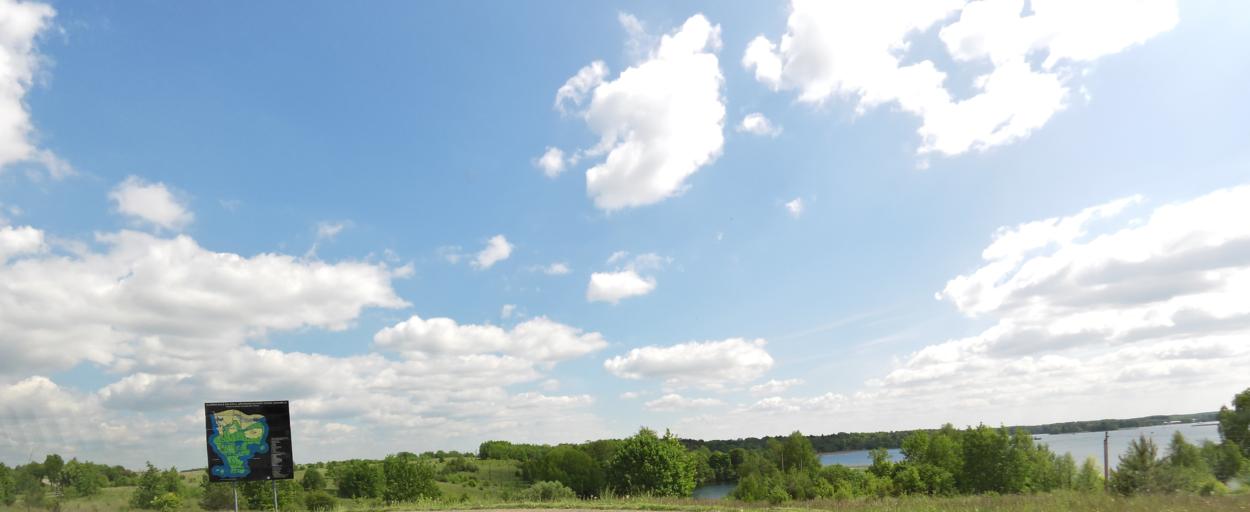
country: LT
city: Trakai
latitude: 54.6731
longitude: 24.9316
